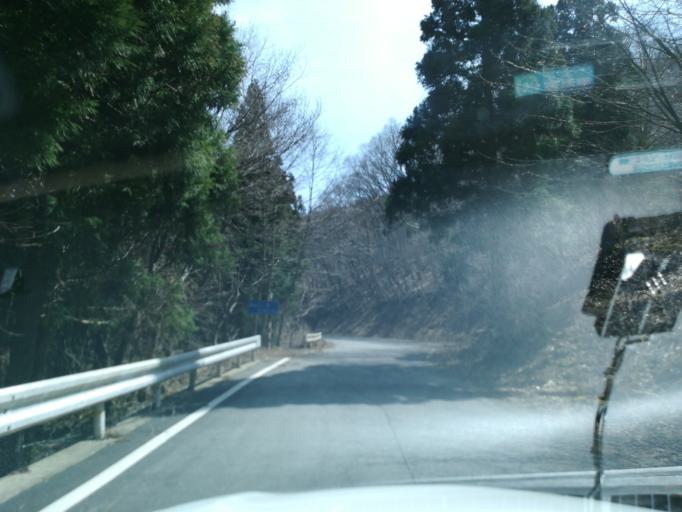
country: JP
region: Tokushima
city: Wakimachi
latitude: 33.8837
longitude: 134.0510
